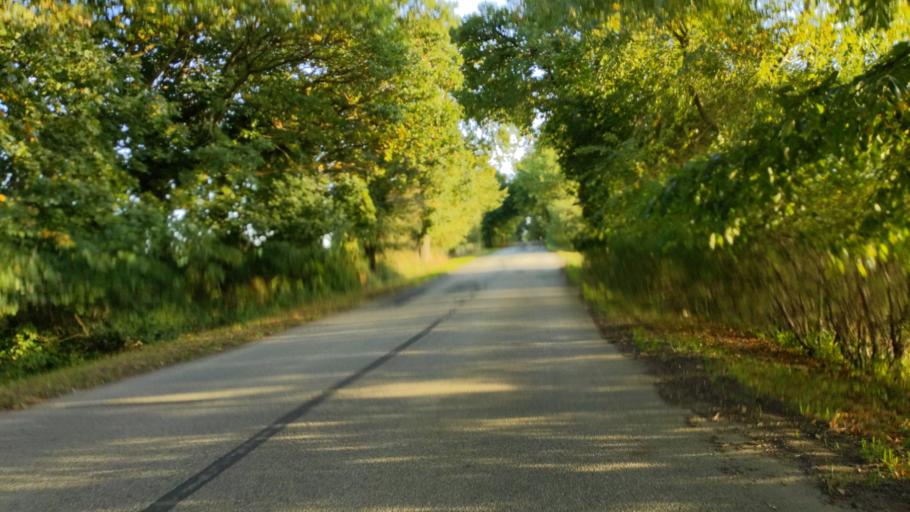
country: DE
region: Schleswig-Holstein
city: Susel
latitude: 54.0675
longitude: 10.7179
